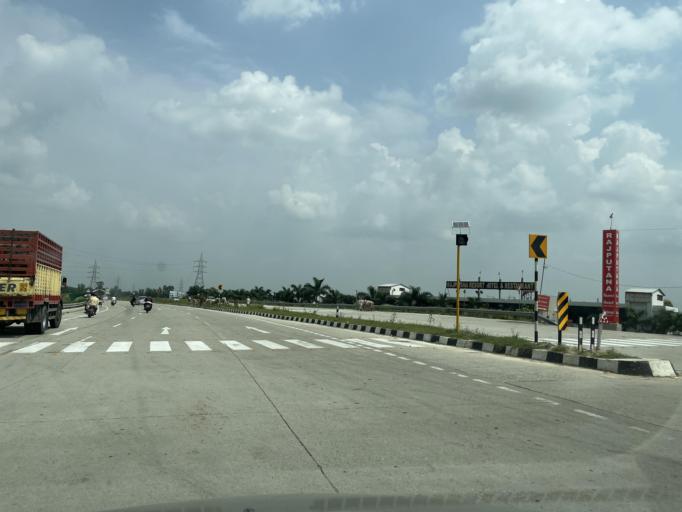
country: IN
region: Uttar Pradesh
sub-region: Bijnor
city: Dhampur
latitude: 29.3165
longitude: 78.5379
